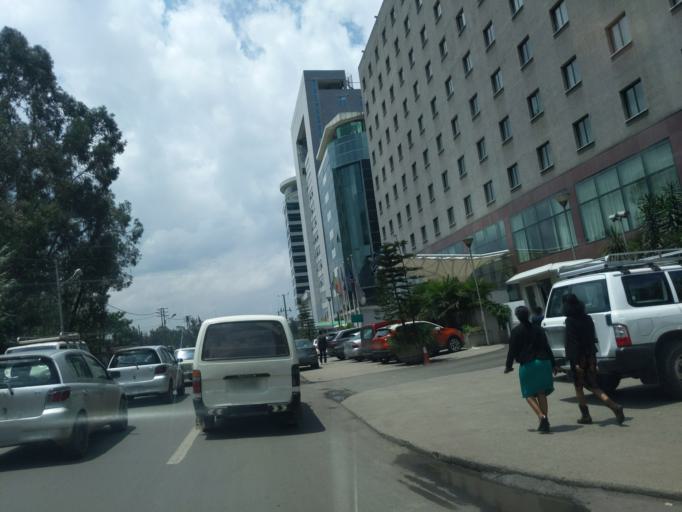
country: ET
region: Adis Abeba
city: Addis Ababa
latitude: 9.0165
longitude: 38.7674
